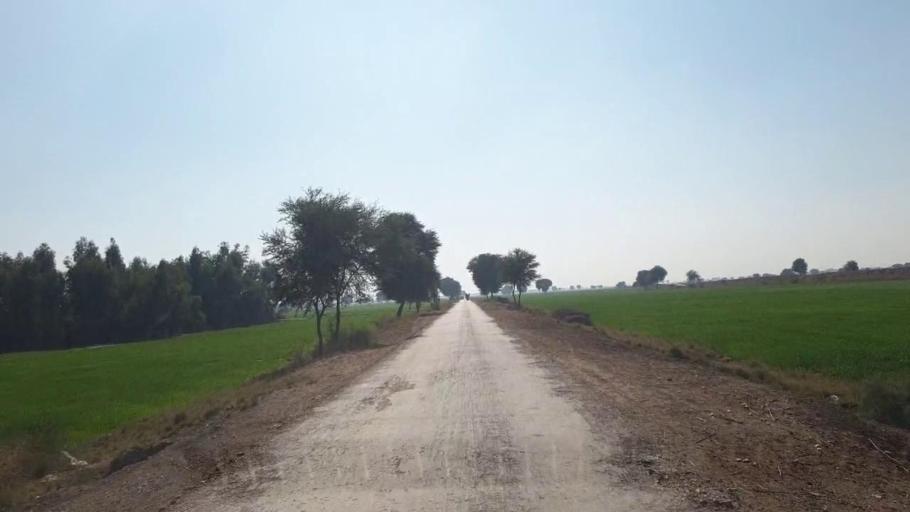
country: PK
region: Sindh
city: Shahpur Chakar
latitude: 26.1165
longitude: 68.6288
